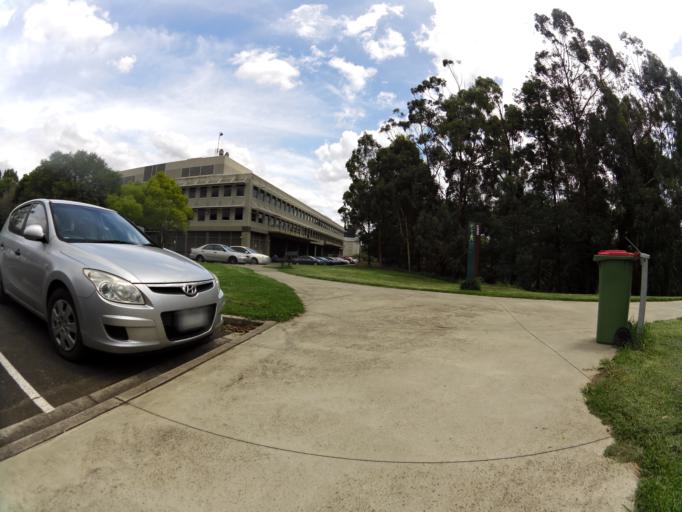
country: AU
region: Victoria
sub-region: Latrobe
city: Traralgon
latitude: -38.1930
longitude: 146.5415
